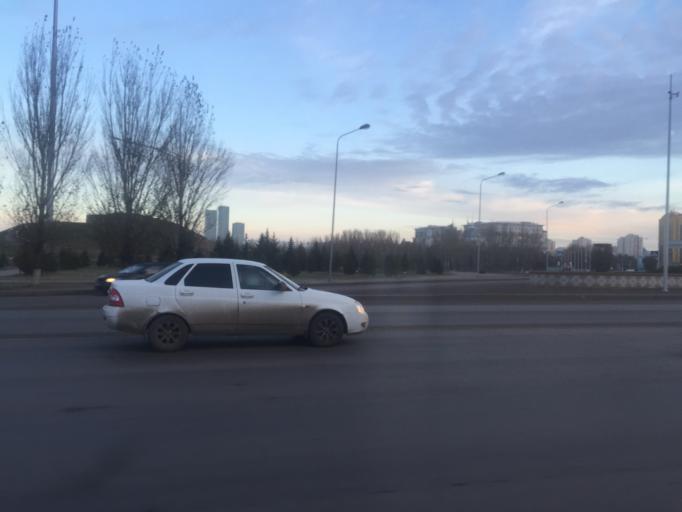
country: KZ
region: Astana Qalasy
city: Astana
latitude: 51.1470
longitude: 71.4216
